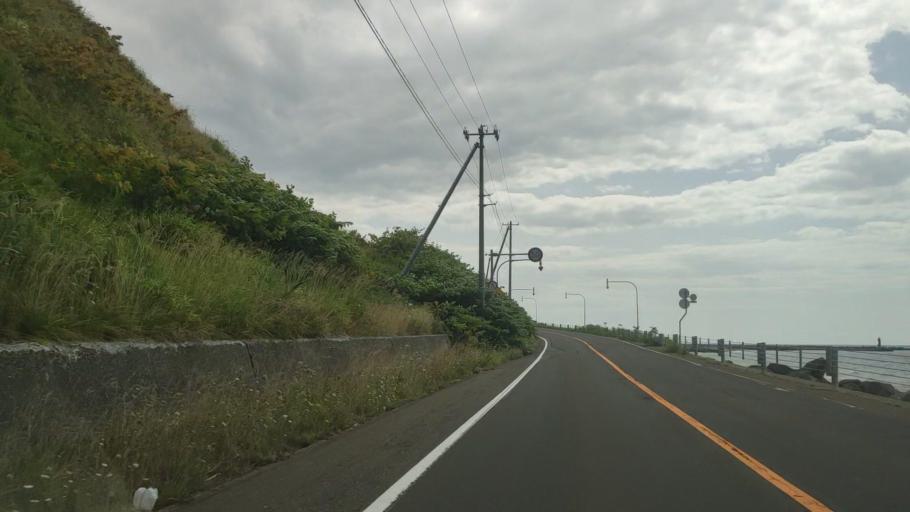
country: JP
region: Hokkaido
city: Rumoi
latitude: 44.5406
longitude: 141.7661
